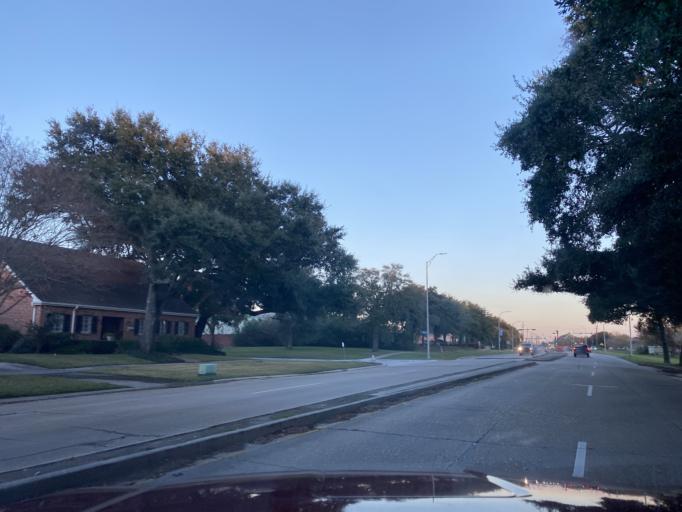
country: US
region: Louisiana
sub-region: Orleans Parish
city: New Orleans
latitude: 30.0257
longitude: -90.0555
